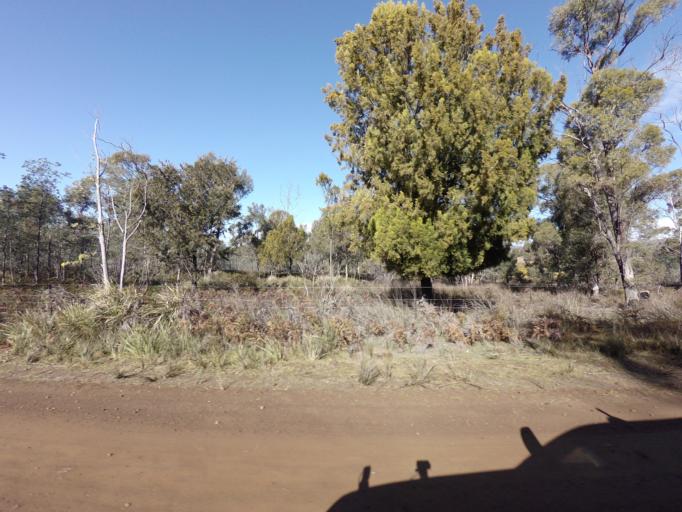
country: AU
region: Tasmania
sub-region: Sorell
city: Sorell
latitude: -42.4041
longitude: 147.9709
